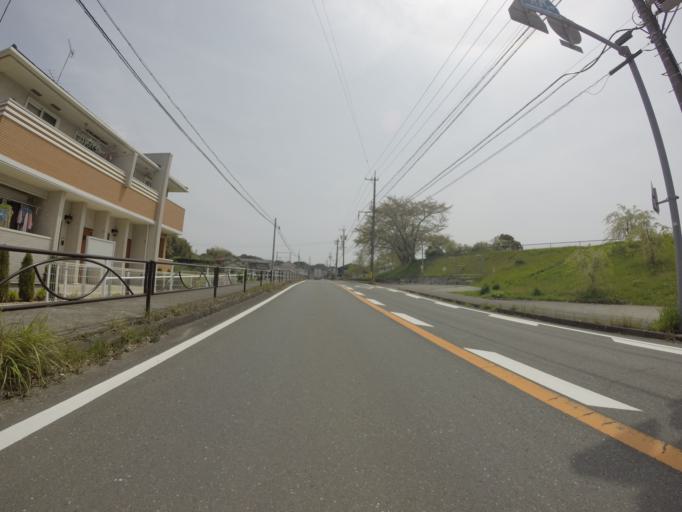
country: JP
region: Shizuoka
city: Kakegawa
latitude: 34.7672
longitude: 138.0278
